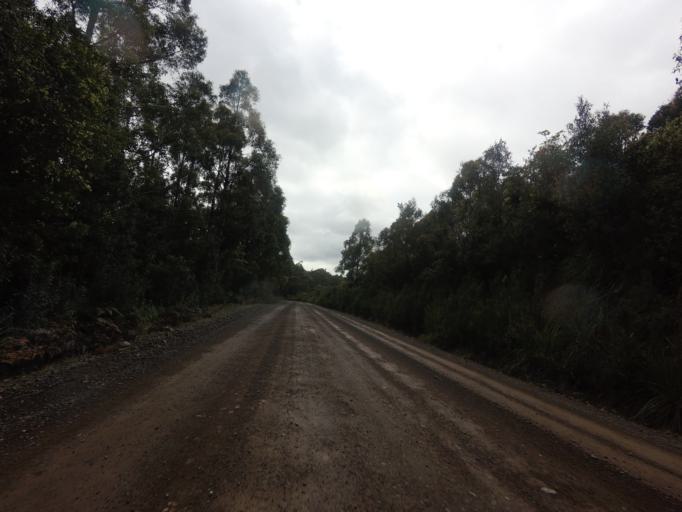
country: AU
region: Tasmania
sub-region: Huon Valley
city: Geeveston
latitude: -43.4677
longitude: 146.8979
